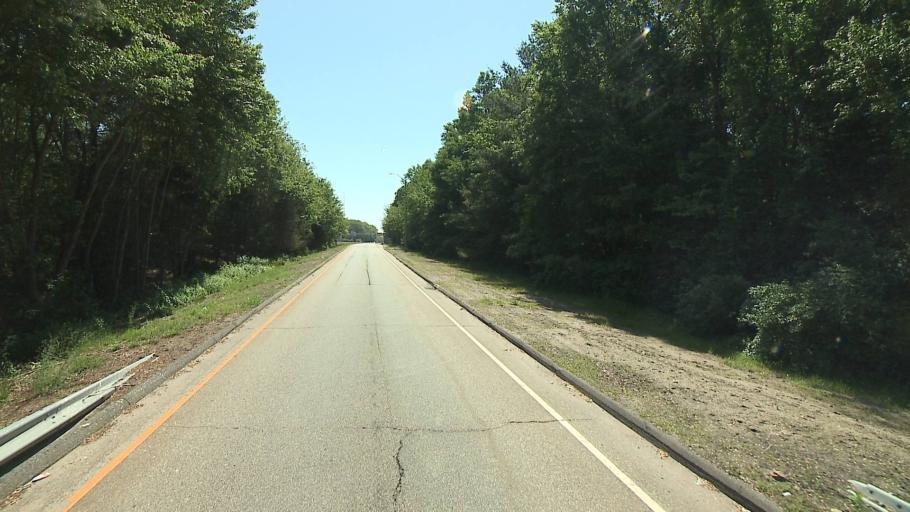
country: US
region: Connecticut
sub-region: New London County
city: Oxoboxo River
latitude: 41.4815
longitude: -72.0981
